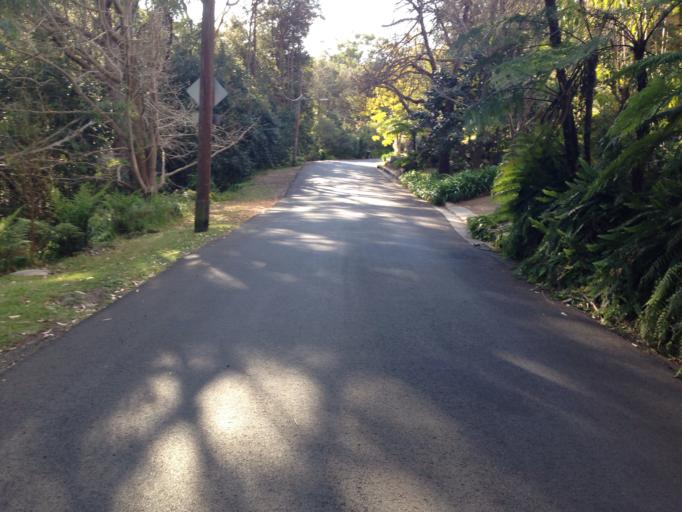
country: AU
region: New South Wales
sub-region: Ku-ring-gai
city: Killara
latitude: -33.7601
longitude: 151.1671
